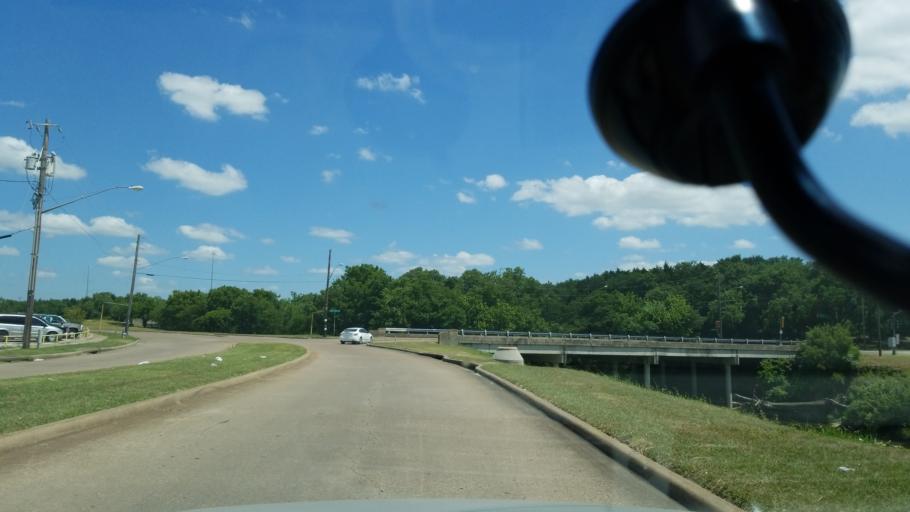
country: US
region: Texas
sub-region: Dallas County
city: Cockrell Hill
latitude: 32.6899
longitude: -96.8288
